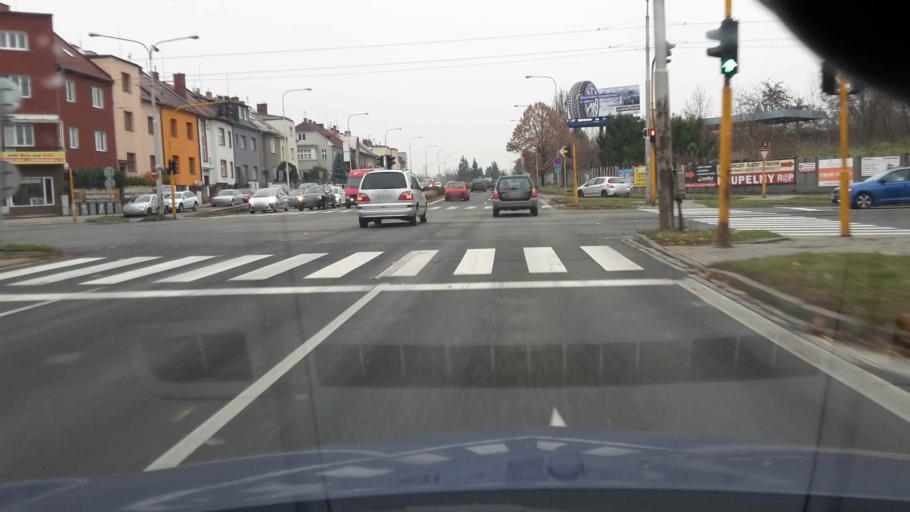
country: CZ
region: Olomoucky
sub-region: Okres Olomouc
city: Olomouc
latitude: 49.5963
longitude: 17.2322
